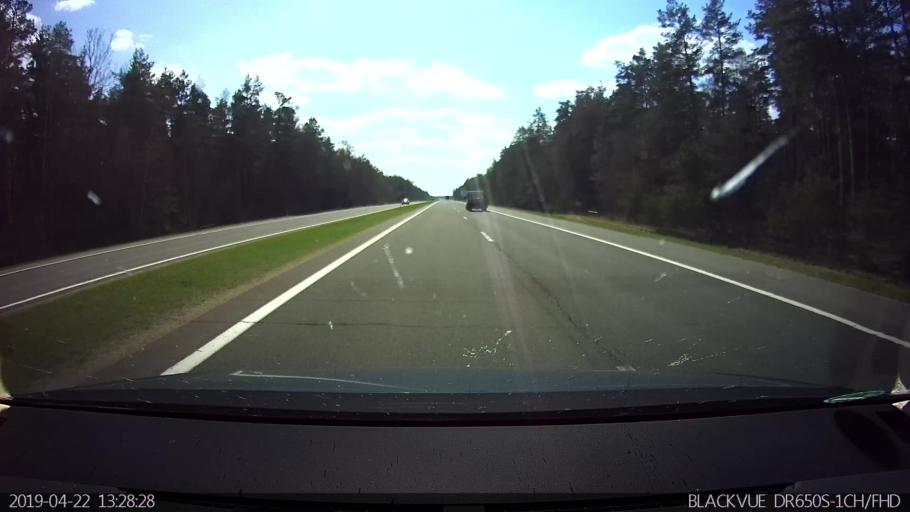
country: BY
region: Brest
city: Baranovichi
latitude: 52.9407
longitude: 25.7068
